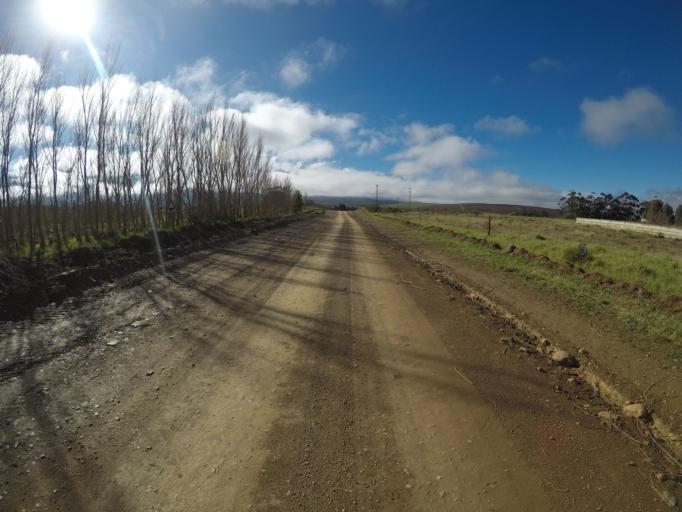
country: ZA
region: Western Cape
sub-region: Overberg District Municipality
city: Caledon
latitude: -34.1145
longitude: 19.7424
